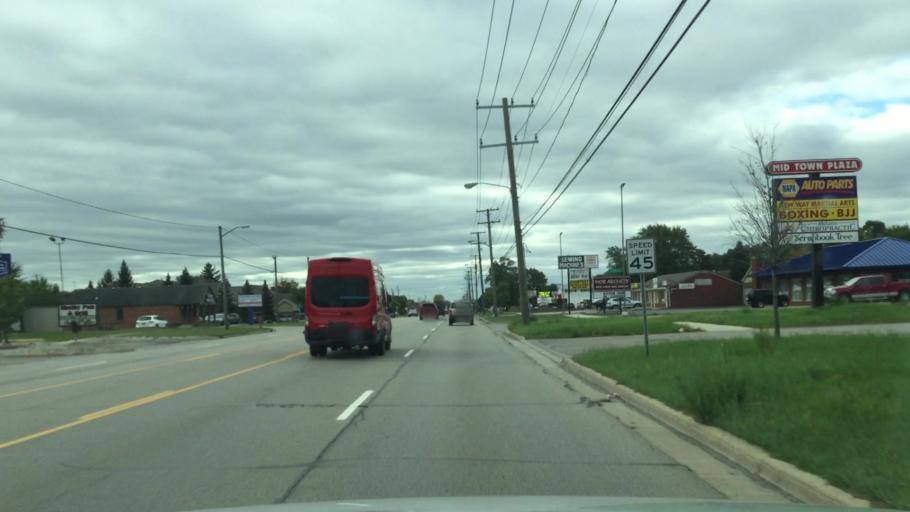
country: US
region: Michigan
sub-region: Macomb County
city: Utica
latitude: 42.6484
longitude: -83.0332
